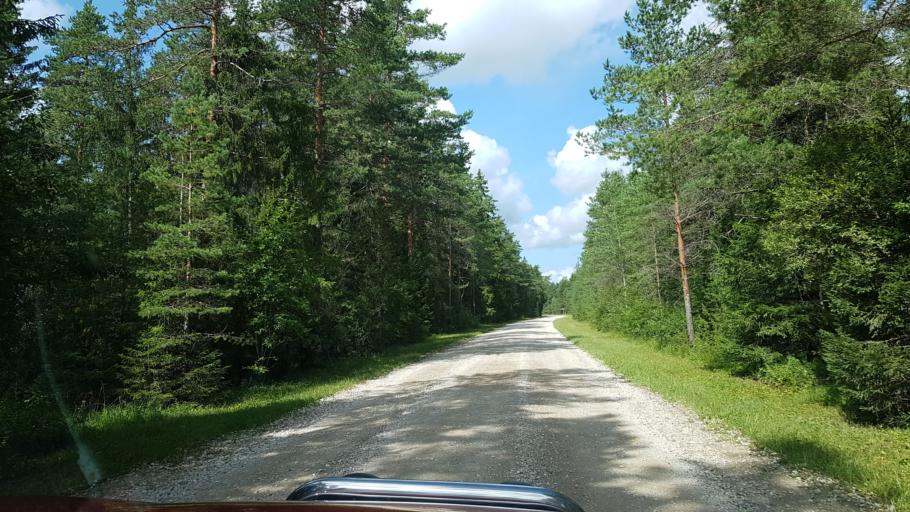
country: EE
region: Raplamaa
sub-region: Rapla vald
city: Rapla
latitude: 58.9595
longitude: 24.6473
